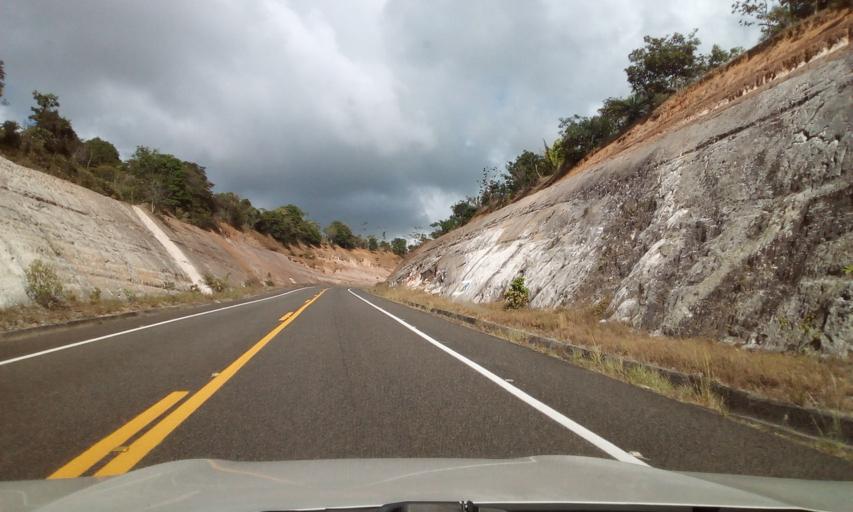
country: BR
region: Sergipe
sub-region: Indiaroba
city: Indiaroba
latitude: -11.5622
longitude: -37.5718
